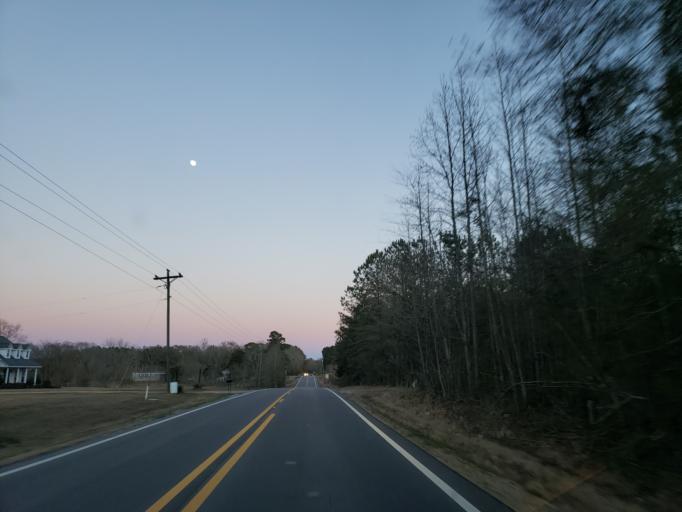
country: US
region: Mississippi
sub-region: Jones County
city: Ellisville
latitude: 31.5798
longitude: -89.2604
